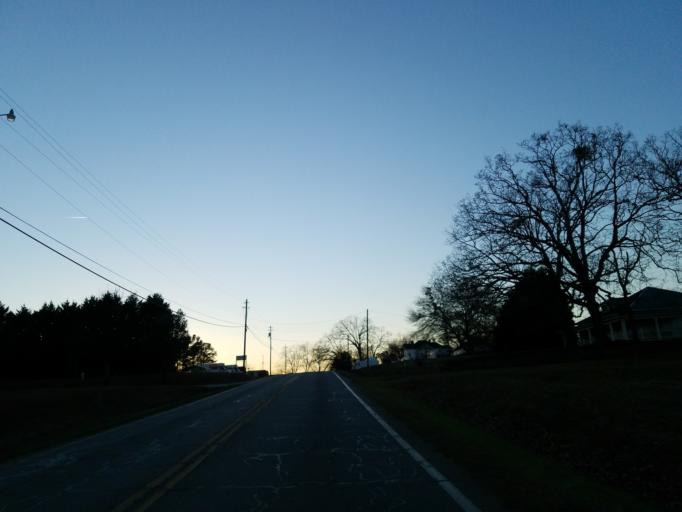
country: US
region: Georgia
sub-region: Monroe County
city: Forsyth
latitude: 33.0269
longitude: -83.9188
